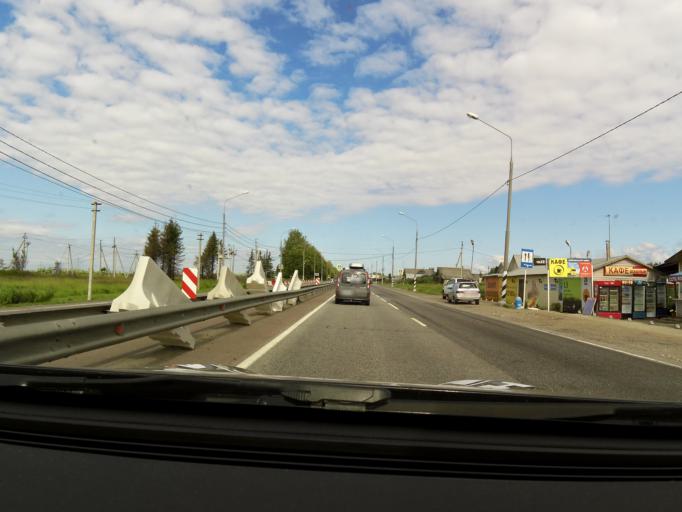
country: RU
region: Tverskaya
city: Gorodnya
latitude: 56.7468
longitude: 36.2208
